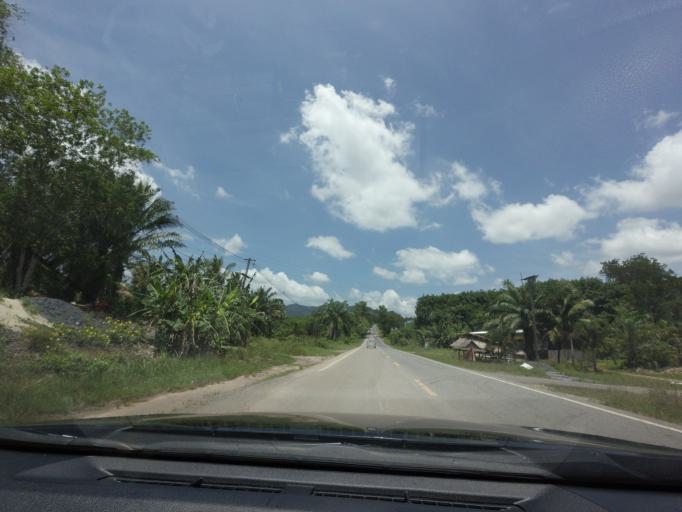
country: TH
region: Chumphon
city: Ban Nam Yuen
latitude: 9.9039
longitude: 98.8970
